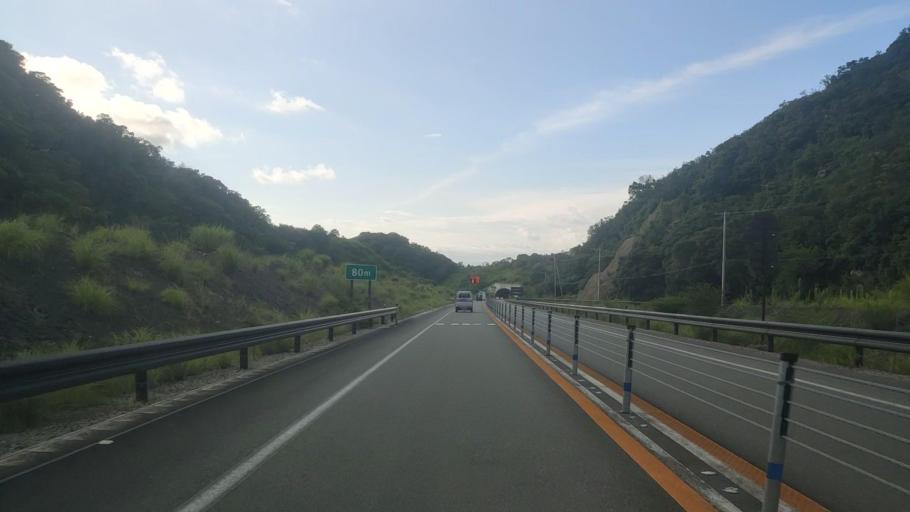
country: JP
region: Wakayama
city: Tanabe
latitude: 33.6353
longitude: 135.4111
